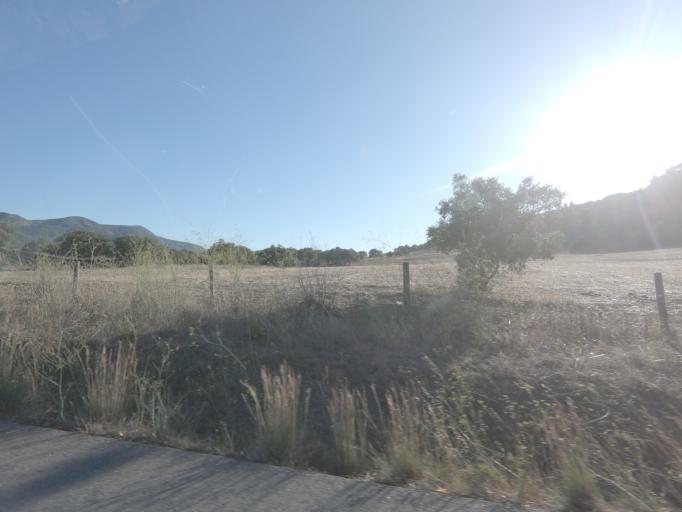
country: PT
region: Setubal
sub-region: Palmela
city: Quinta do Anjo
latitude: 38.5189
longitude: -8.9818
